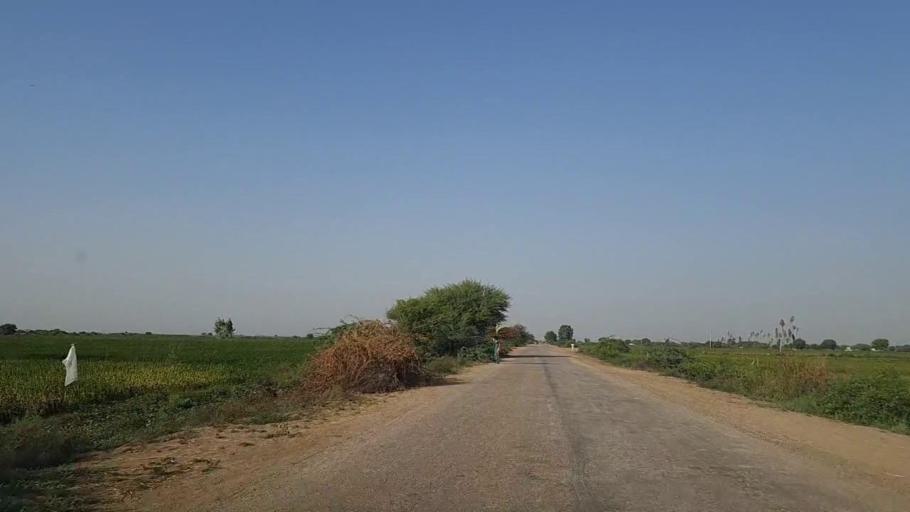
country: PK
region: Sindh
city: Mirpur Batoro
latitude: 24.5835
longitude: 68.3965
